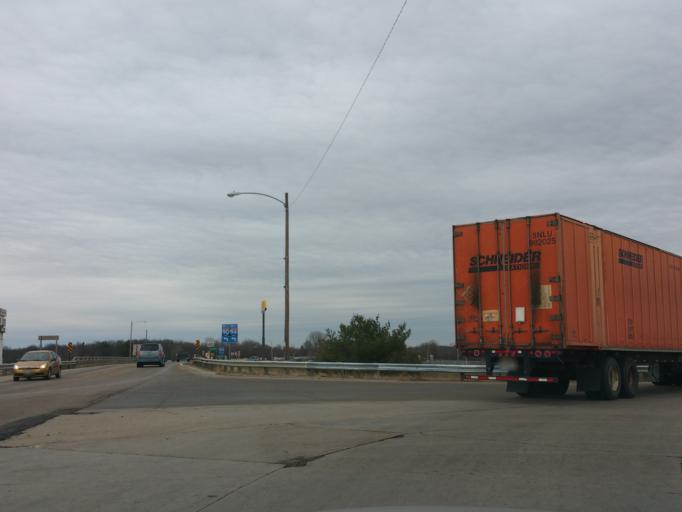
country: US
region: Wisconsin
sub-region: Juneau County
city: New Lisbon
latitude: 43.8824
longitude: -90.1483
